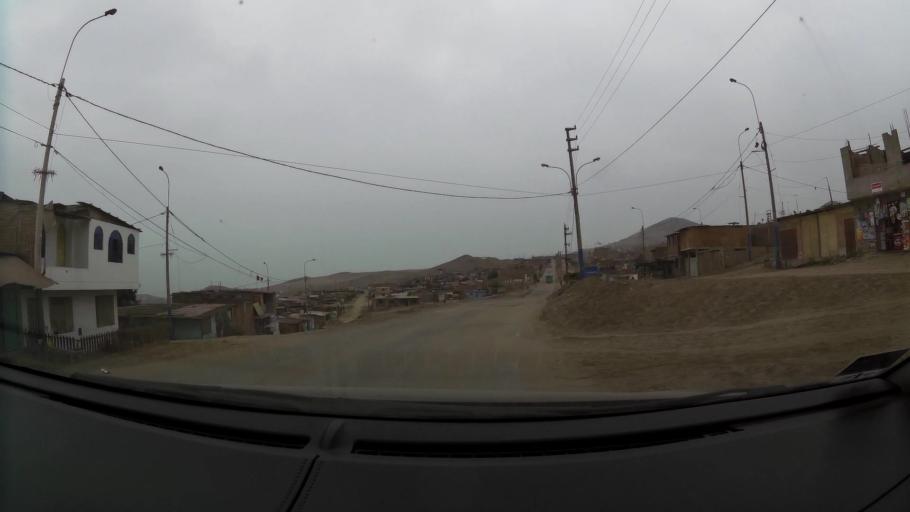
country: PE
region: Lima
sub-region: Lima
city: Santa Rosa
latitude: -11.8371
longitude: -77.1619
